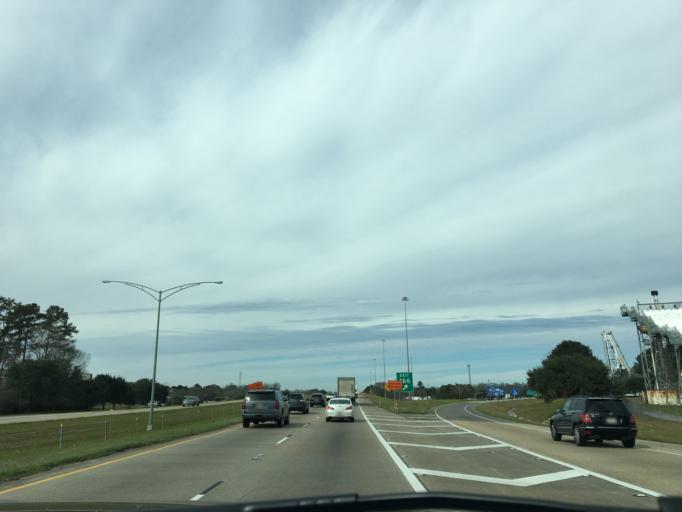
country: US
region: Louisiana
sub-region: East Baton Rouge Parish
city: Old Jefferson
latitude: 30.3436
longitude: -91.0271
